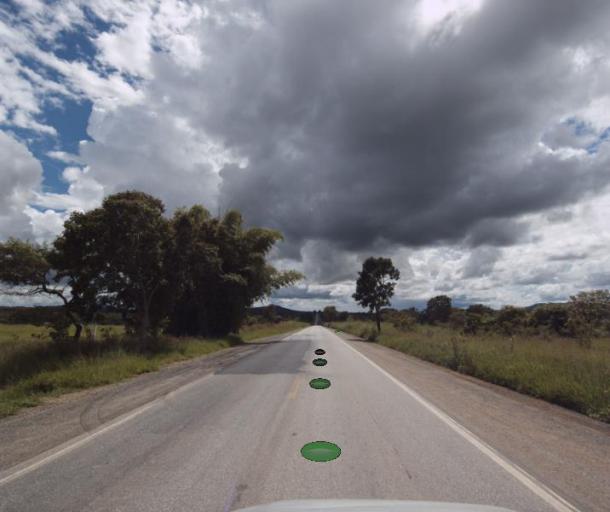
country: BR
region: Goias
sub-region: Uruacu
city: Uruacu
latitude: -14.2721
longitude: -49.1457
